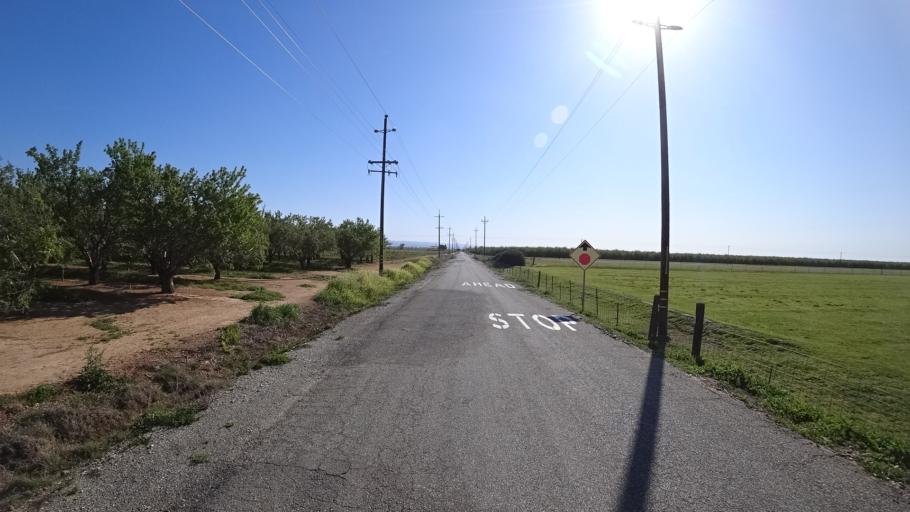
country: US
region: California
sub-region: Glenn County
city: Hamilton City
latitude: 39.7757
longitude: -122.0684
